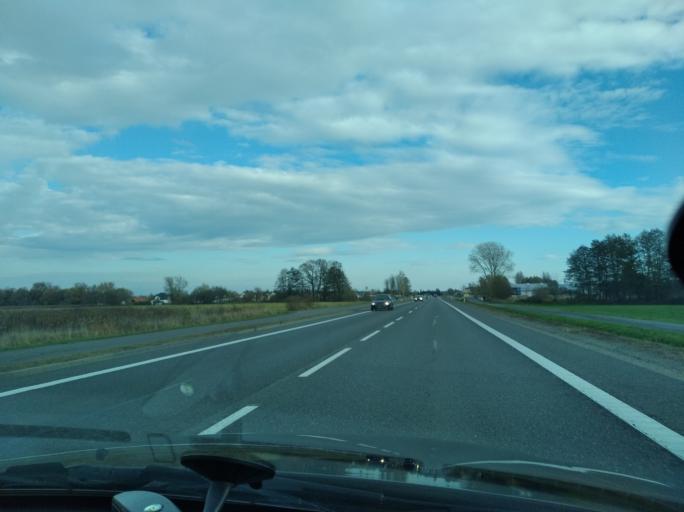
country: PL
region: Subcarpathian Voivodeship
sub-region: Powiat debicki
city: Debica
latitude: 50.0476
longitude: 21.4422
